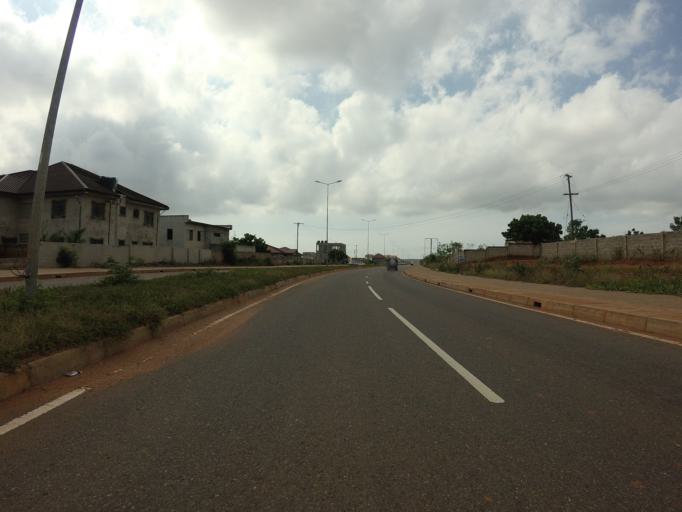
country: GH
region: Greater Accra
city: Teshi Old Town
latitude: 5.6062
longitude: -0.1394
